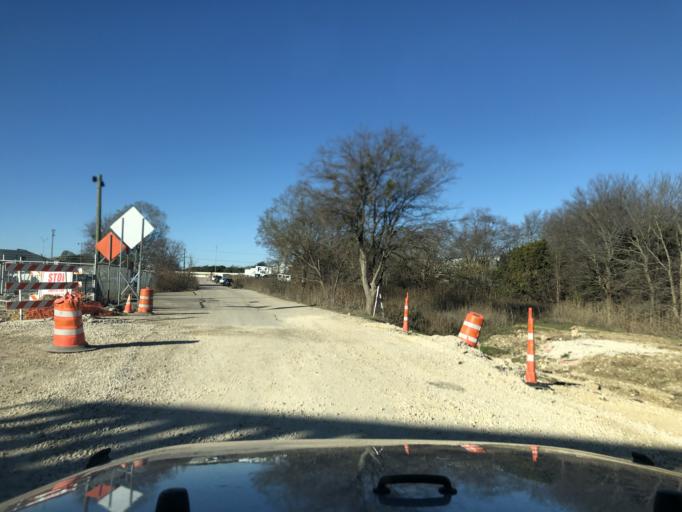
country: US
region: Texas
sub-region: Williamson County
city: Round Rock
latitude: 30.5449
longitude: -97.6893
